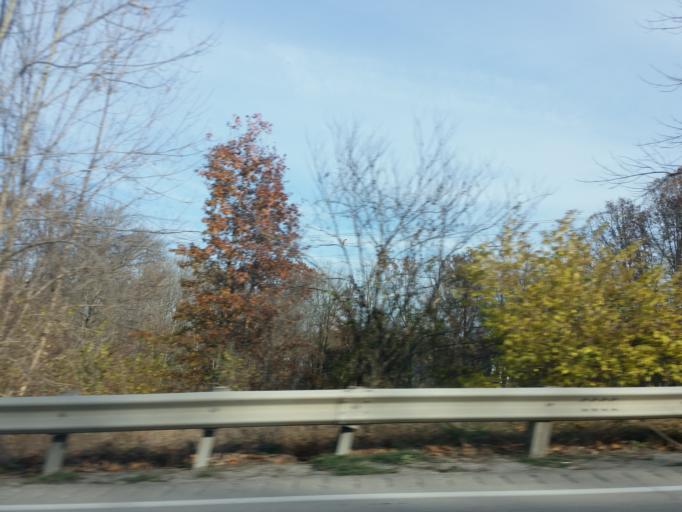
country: US
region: Kentucky
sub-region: Campbell County
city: Claryville
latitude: 38.8317
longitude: -84.3655
